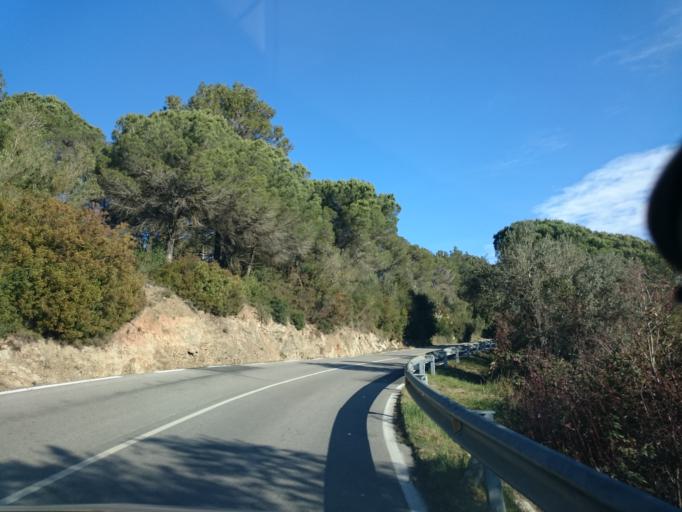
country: ES
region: Catalonia
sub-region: Provincia de Barcelona
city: Molins de Rei
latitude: 41.4241
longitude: 2.0321
